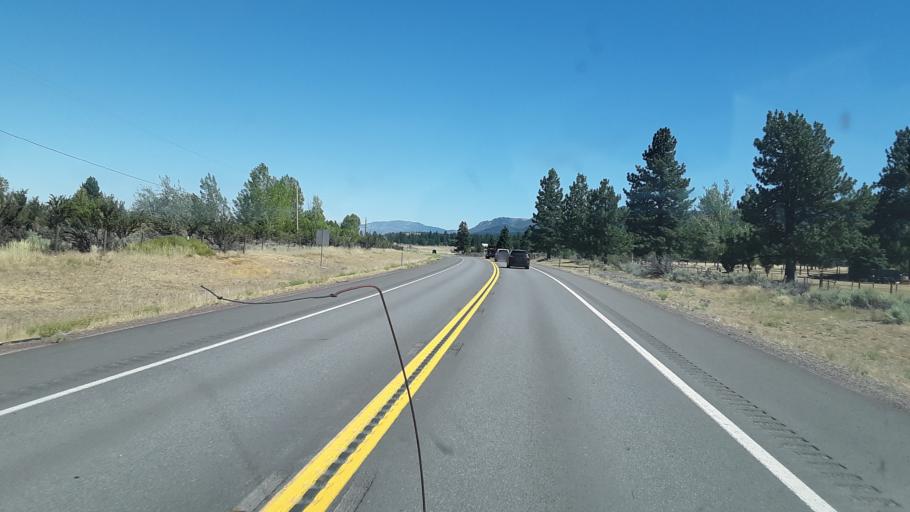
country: US
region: California
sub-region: Lassen County
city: Janesville
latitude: 40.3177
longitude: -120.5428
